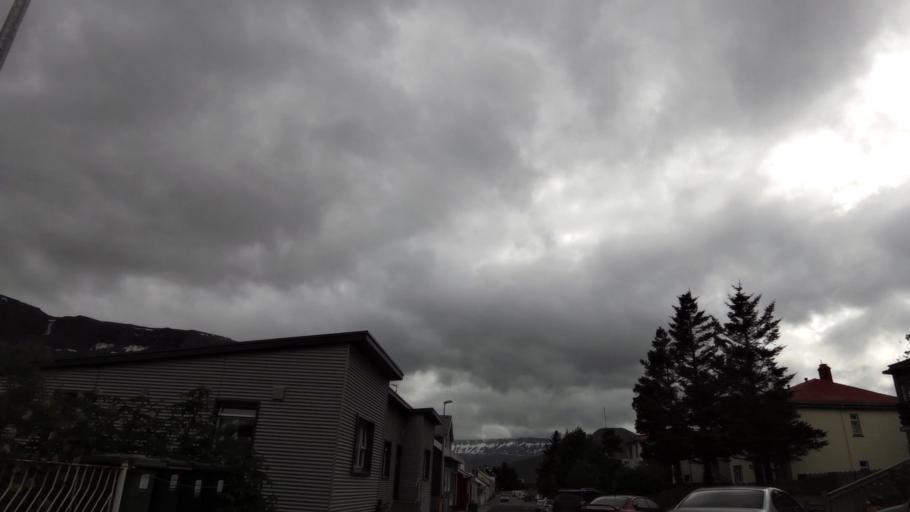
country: IS
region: Westfjords
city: Isafjoerdur
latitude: 66.0779
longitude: -23.1275
